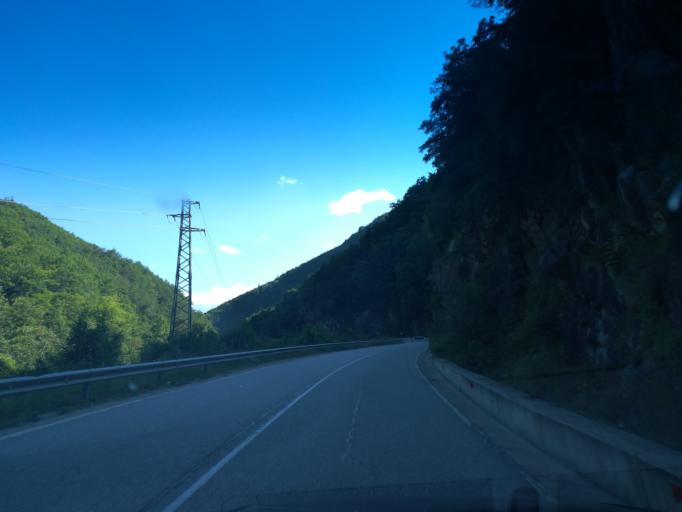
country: BG
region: Smolyan
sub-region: Obshtina Chepelare
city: Chepelare
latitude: 41.7868
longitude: 24.7094
